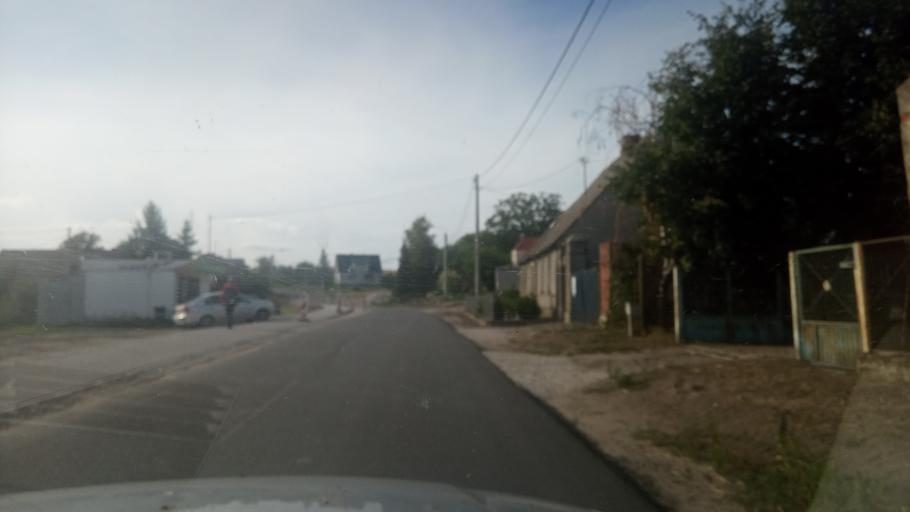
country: PL
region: Kujawsko-Pomorskie
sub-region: Powiat nakielski
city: Sadki
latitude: 53.1955
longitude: 17.3883
